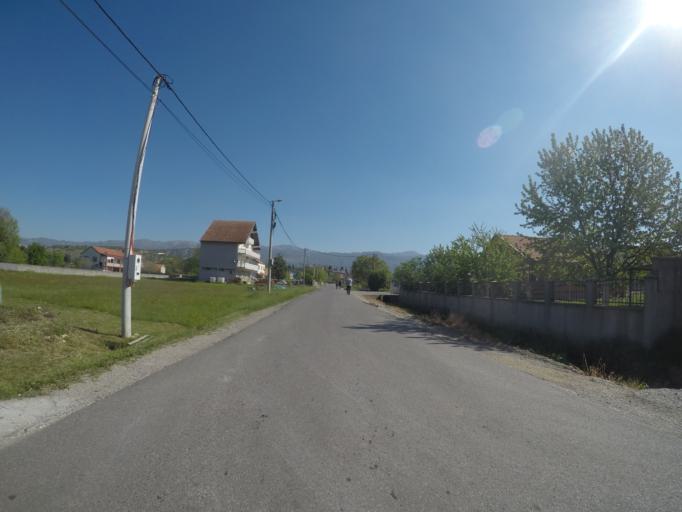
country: ME
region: Danilovgrad
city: Danilovgrad
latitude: 42.5445
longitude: 19.0978
